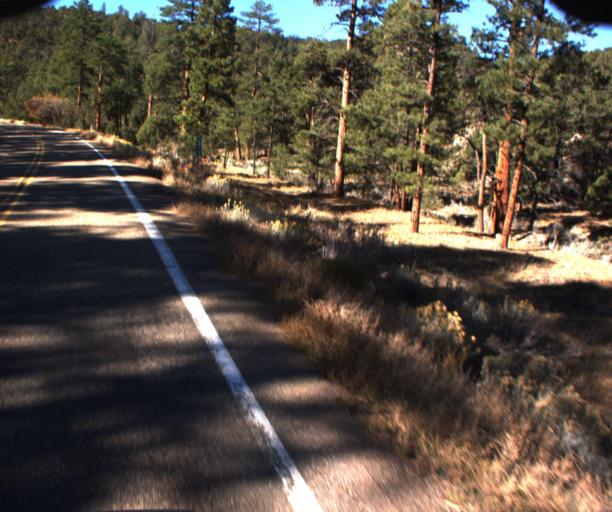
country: US
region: Arizona
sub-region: Coconino County
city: Fredonia
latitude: 36.7384
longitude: -112.1265
